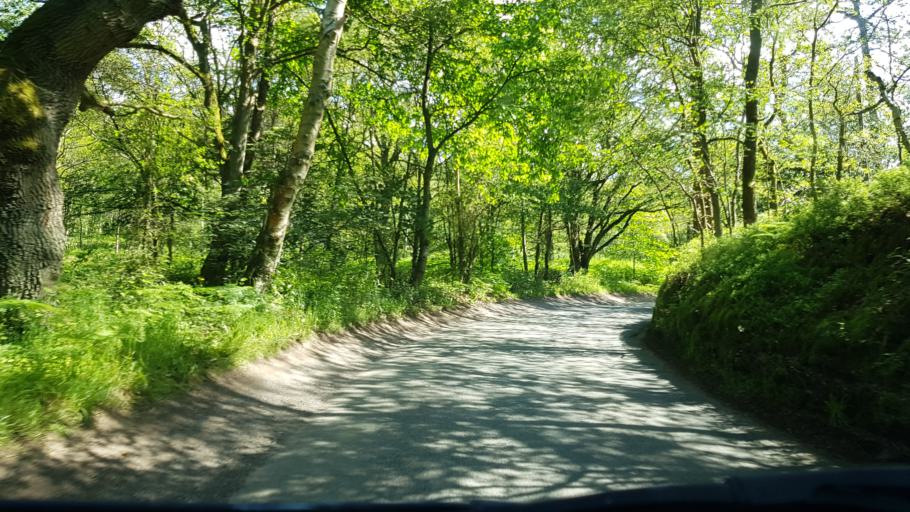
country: GB
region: England
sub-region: Worcestershire
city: Kidderminster
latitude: 52.4445
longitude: -2.2559
